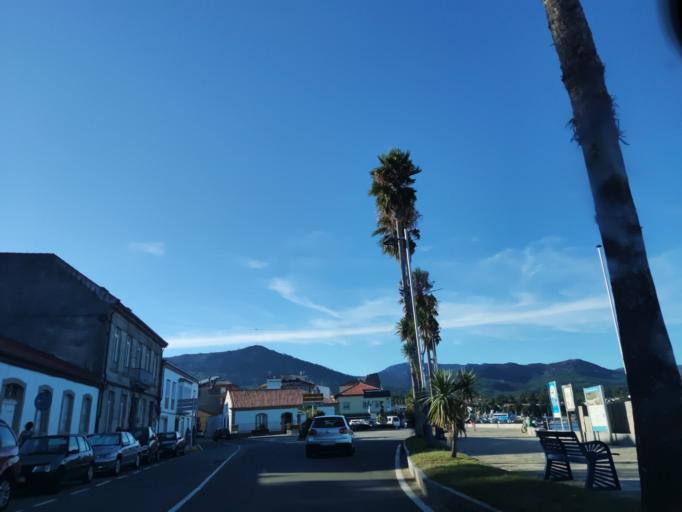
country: ES
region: Galicia
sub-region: Provincia da Coruna
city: Boiro
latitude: 42.6012
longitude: -8.9359
